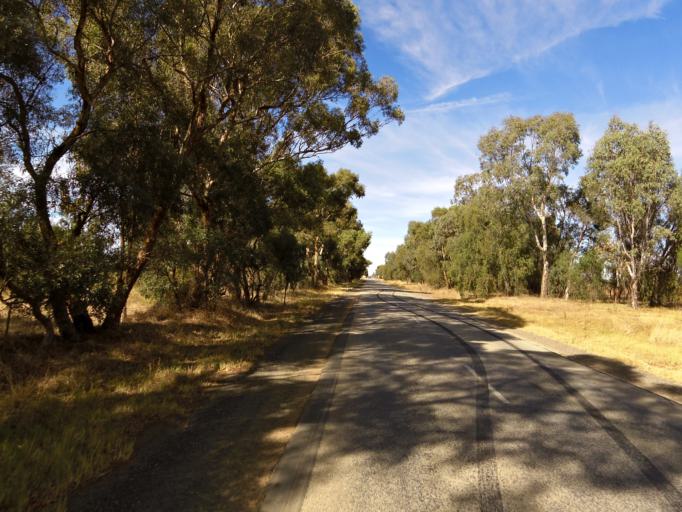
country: AU
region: Victoria
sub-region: Campaspe
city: Echuca
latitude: -36.2575
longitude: 144.5358
